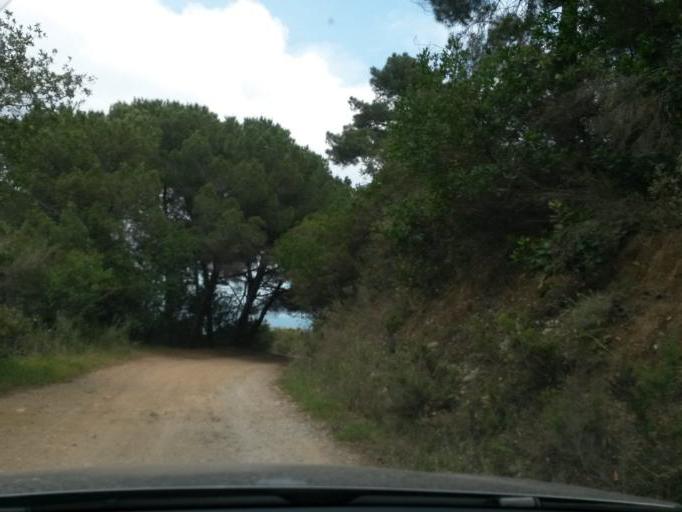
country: IT
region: Tuscany
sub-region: Provincia di Livorno
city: Porto Azzurro
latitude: 42.7428
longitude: 10.4086
